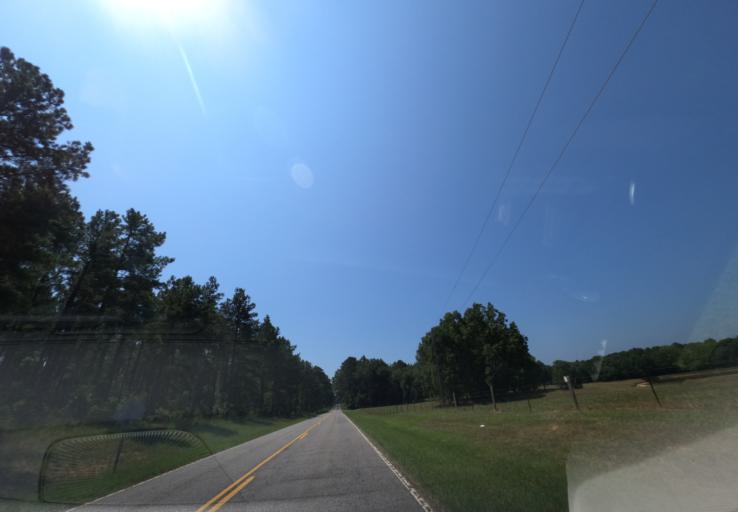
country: US
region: South Carolina
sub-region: McCormick County
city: McCormick
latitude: 33.9857
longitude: -82.1299
